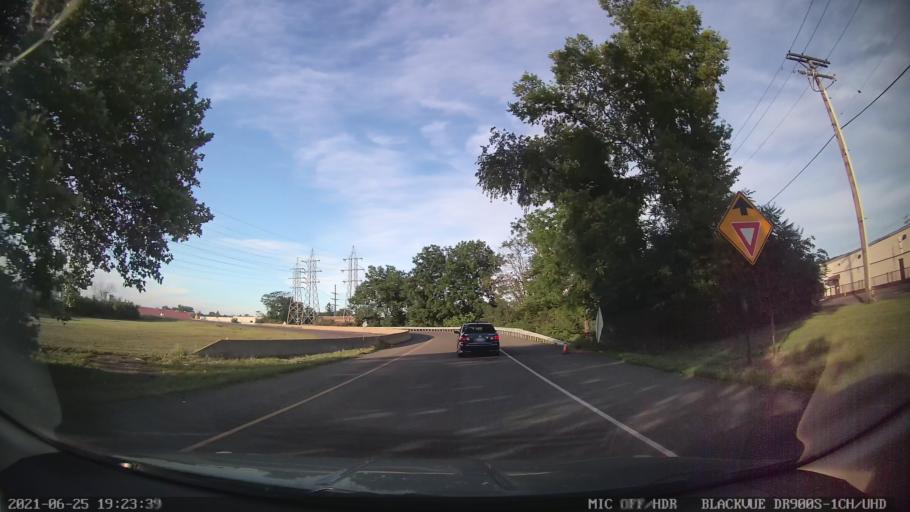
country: US
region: Pennsylvania
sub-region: Berks County
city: Hyde Park
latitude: 40.3686
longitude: -75.9325
